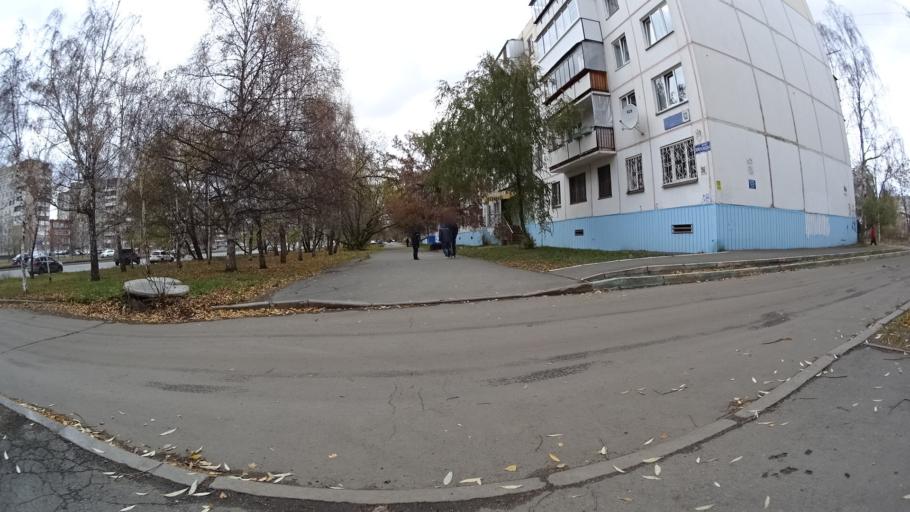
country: RU
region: Chelyabinsk
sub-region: Gorod Chelyabinsk
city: Chelyabinsk
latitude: 55.1894
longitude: 61.3160
